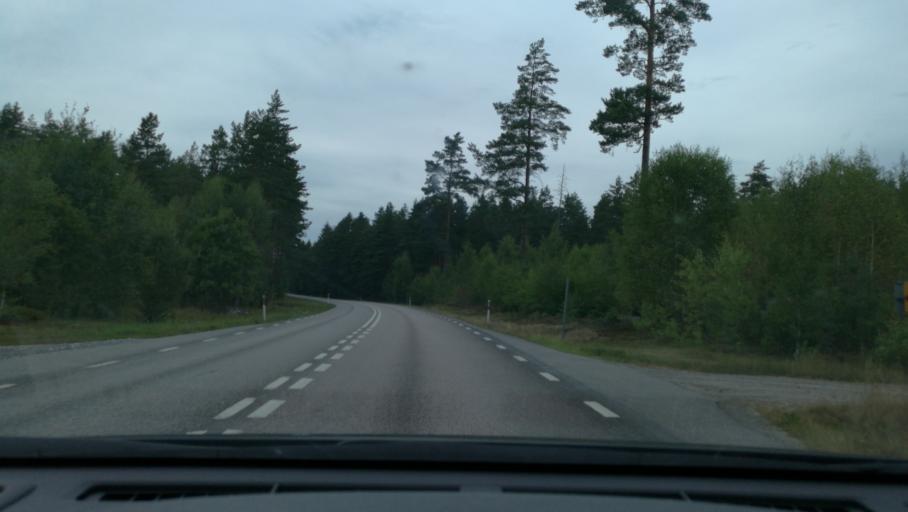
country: SE
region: Soedermanland
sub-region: Katrineholms Kommun
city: Katrineholm
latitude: 59.1283
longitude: 16.1509
